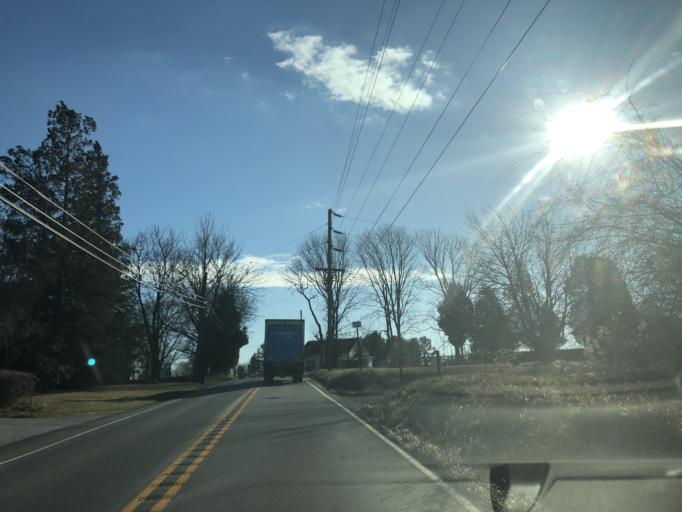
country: US
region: Pennsylvania
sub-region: Chester County
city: South Coatesville
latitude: 39.9492
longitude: -75.8412
